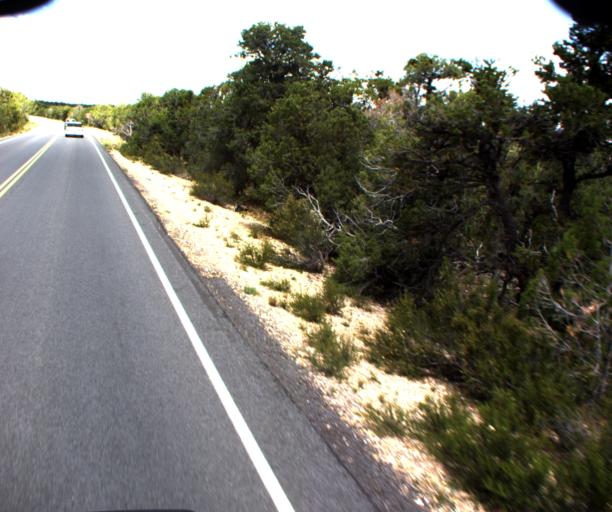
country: US
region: Arizona
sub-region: Coconino County
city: Grand Canyon
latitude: 36.0271
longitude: -111.8272
